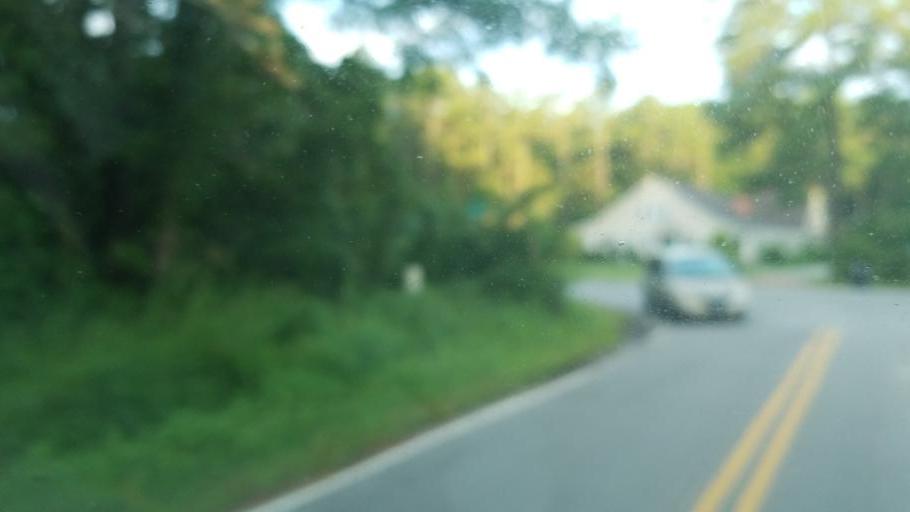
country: US
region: North Carolina
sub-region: Dare County
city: Wanchese
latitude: 35.8434
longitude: -75.6421
